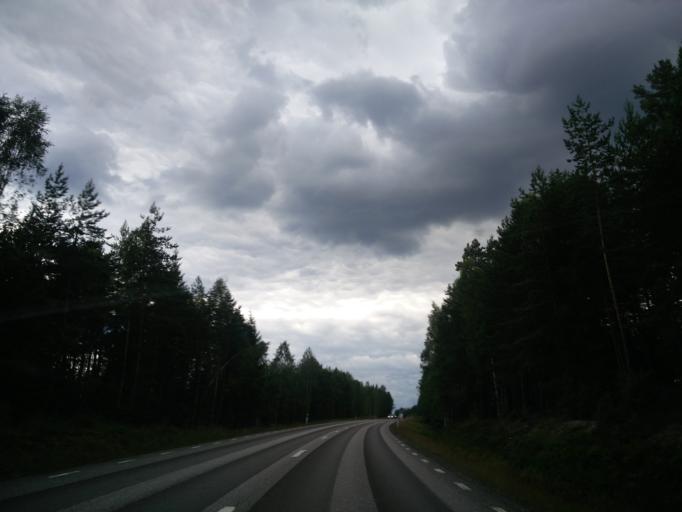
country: SE
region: OErebro
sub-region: Hallefors Kommun
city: Haellefors
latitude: 59.7854
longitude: 14.3541
